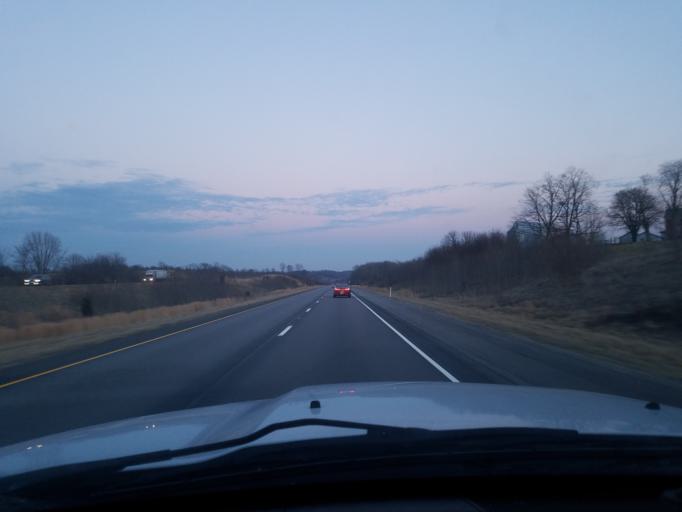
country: US
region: Indiana
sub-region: Dubois County
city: Ferdinand
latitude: 38.2031
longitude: -86.8231
